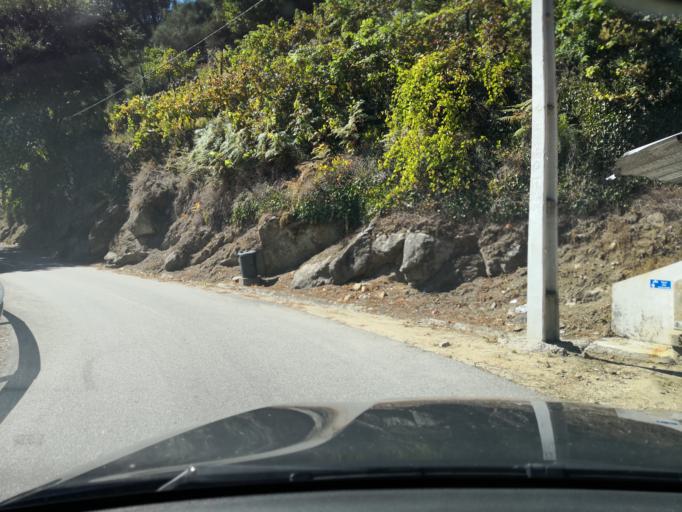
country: PT
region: Vila Real
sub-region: Santa Marta de Penaguiao
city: Santa Marta de Penaguiao
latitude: 41.2566
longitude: -7.8061
